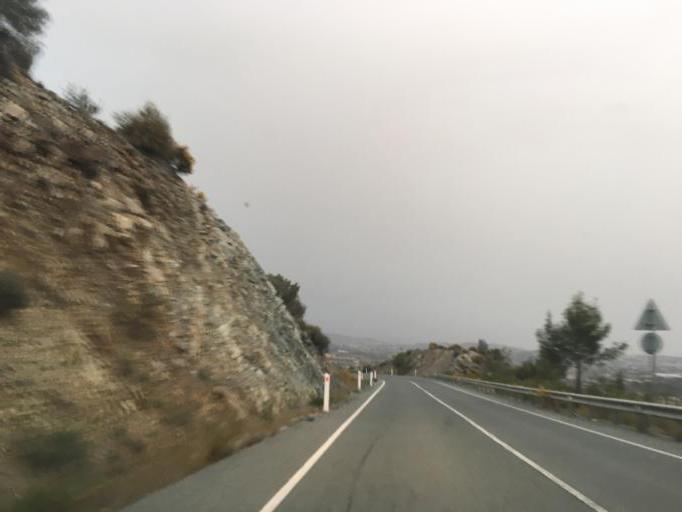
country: CY
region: Limassol
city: Parekklisha
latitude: 34.7889
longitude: 33.1601
